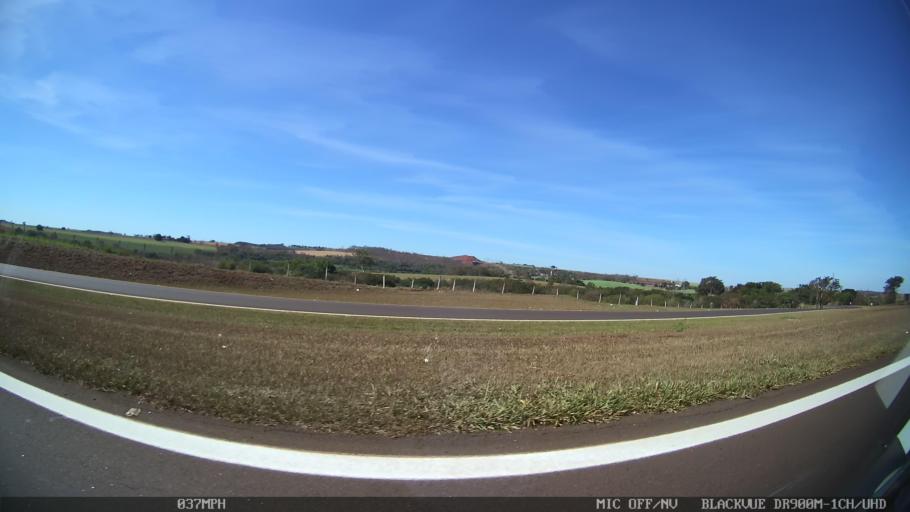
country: BR
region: Sao Paulo
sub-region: Sao Joaquim Da Barra
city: Sao Joaquim da Barra
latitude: -20.5247
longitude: -47.8397
